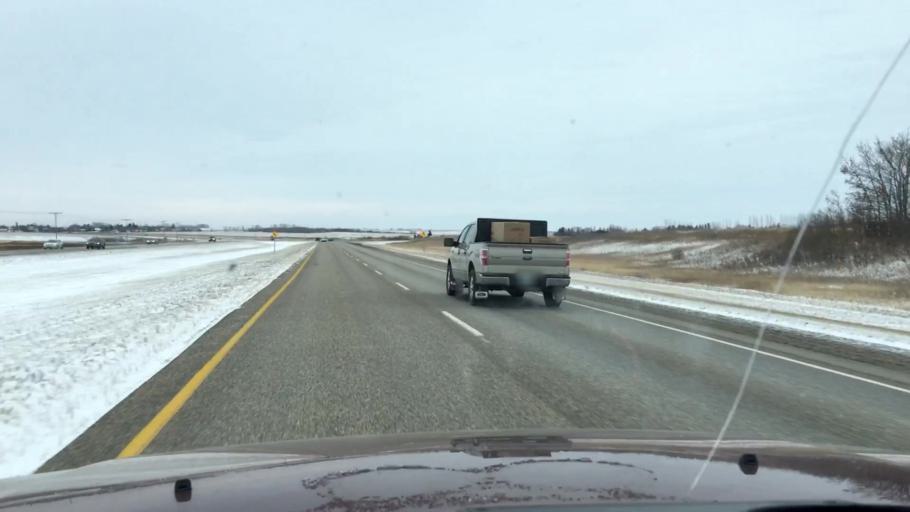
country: CA
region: Saskatchewan
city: Moose Jaw
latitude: 50.9532
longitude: -105.7093
